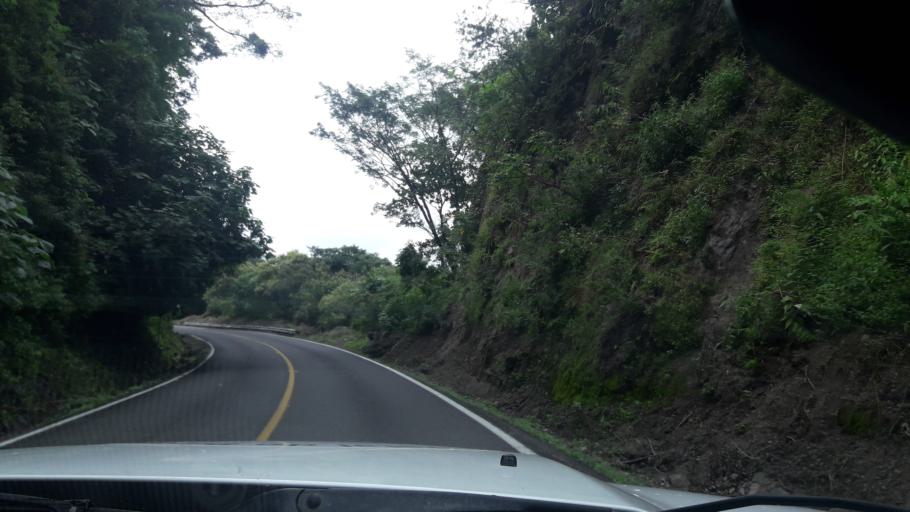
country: MX
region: Colima
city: Suchitlan
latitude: 19.4383
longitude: -103.7124
